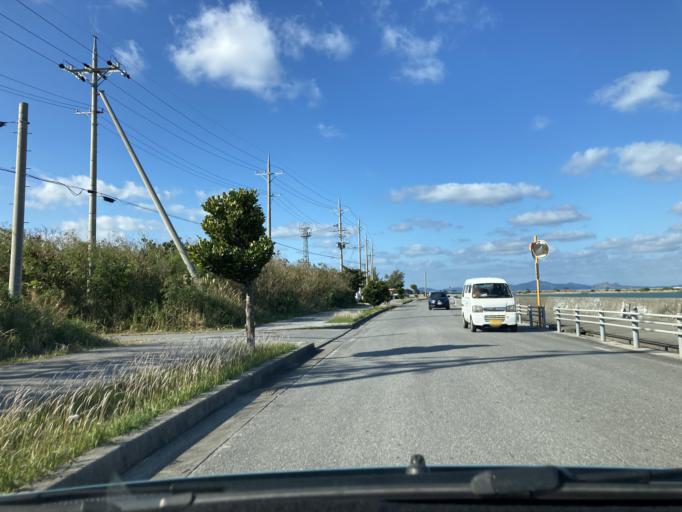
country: JP
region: Okinawa
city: Katsuren-haebaru
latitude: 26.3240
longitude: 127.9131
